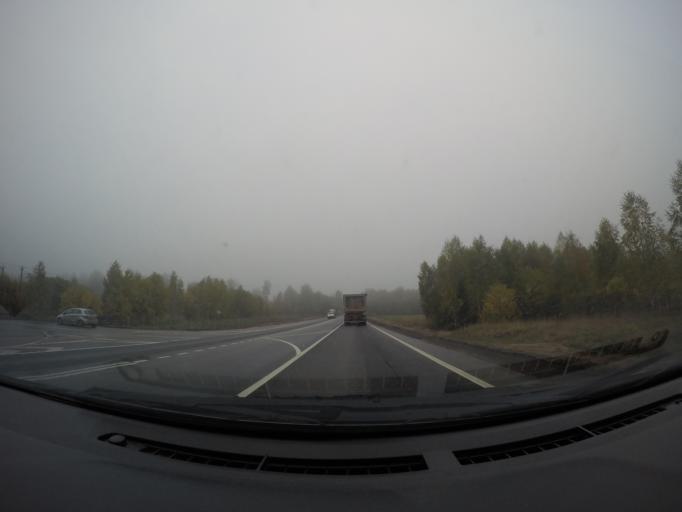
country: RU
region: Moskovskaya
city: Rumyantsevo
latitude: 55.8642
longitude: 36.5343
